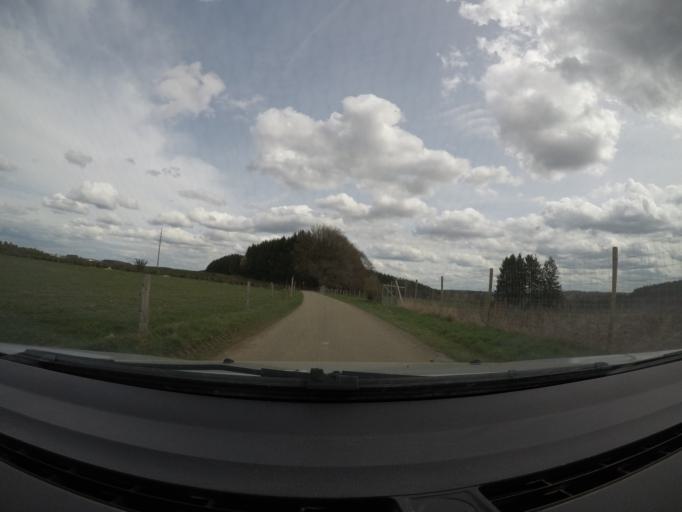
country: BE
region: Wallonia
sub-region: Province du Luxembourg
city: Leglise
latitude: 49.7957
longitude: 5.4870
